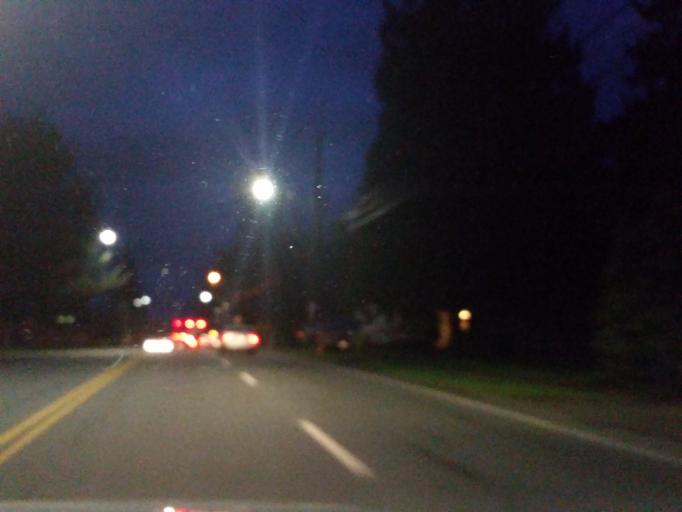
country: US
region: Washington
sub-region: King County
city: Shoreline
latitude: 47.7232
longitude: -122.3315
